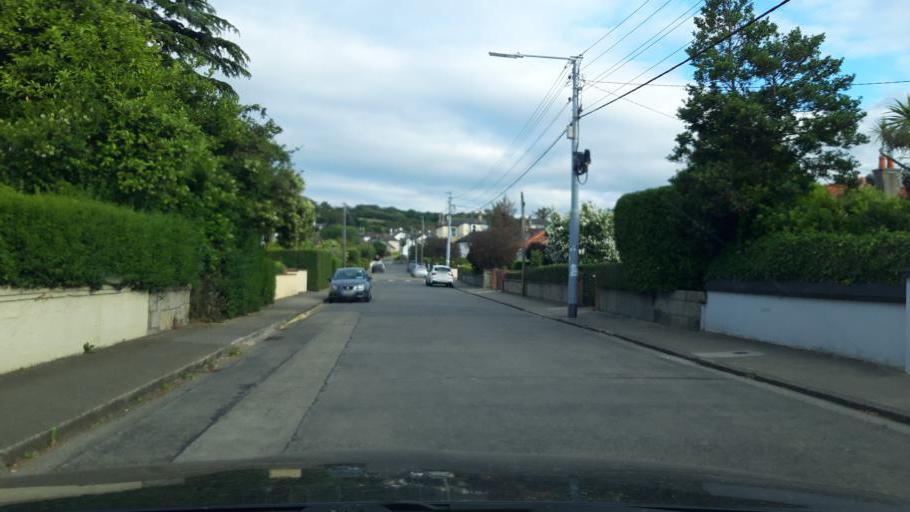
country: IE
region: Leinster
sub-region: Wicklow
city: Bray
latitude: 53.1971
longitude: -6.0998
